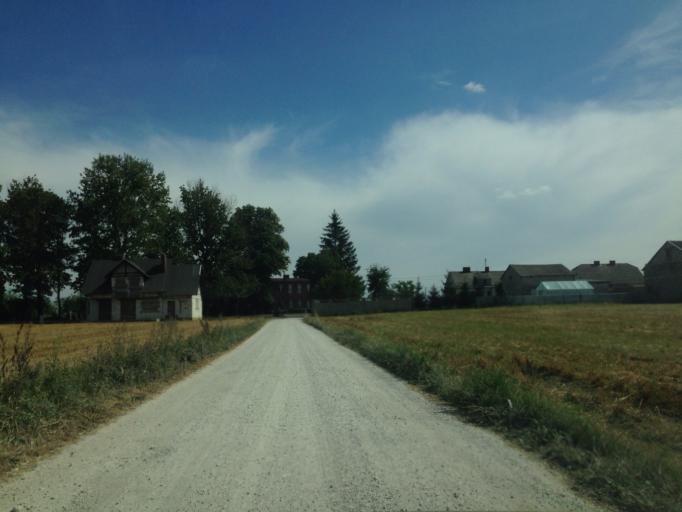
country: PL
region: Kujawsko-Pomorskie
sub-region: Powiat brodnicki
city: Bartniczka
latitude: 53.2291
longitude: 19.5985
